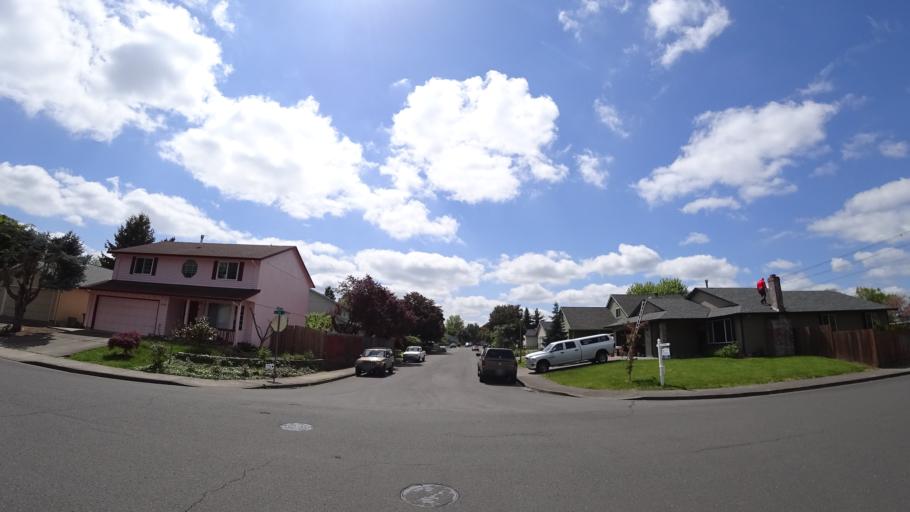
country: US
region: Oregon
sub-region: Washington County
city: Aloha
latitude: 45.5103
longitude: -122.8959
